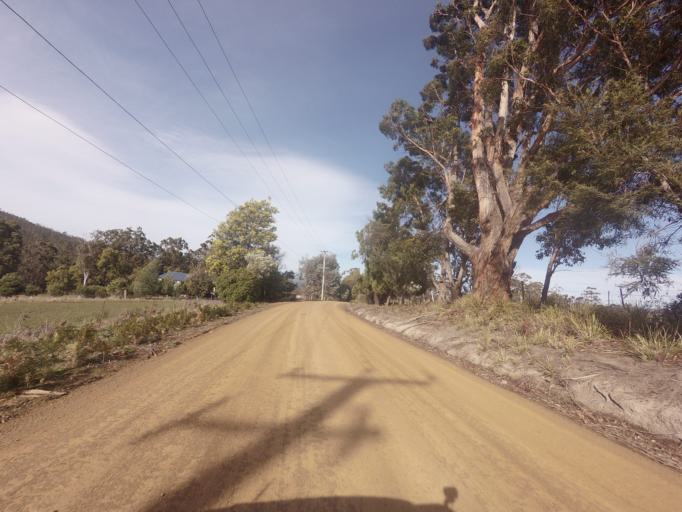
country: AU
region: Tasmania
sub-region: Kingborough
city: Kettering
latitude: -43.0993
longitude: 147.2639
